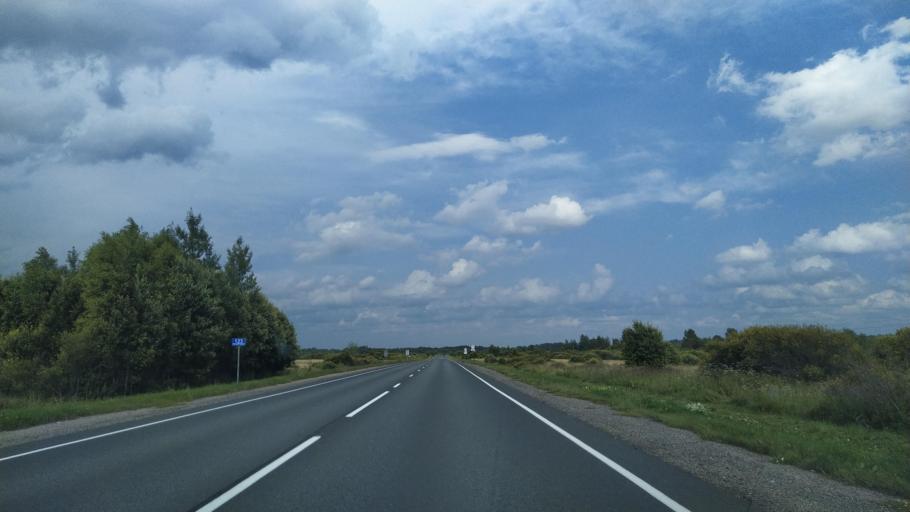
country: RU
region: Pskov
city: Porkhov
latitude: 57.9667
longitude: 29.6838
